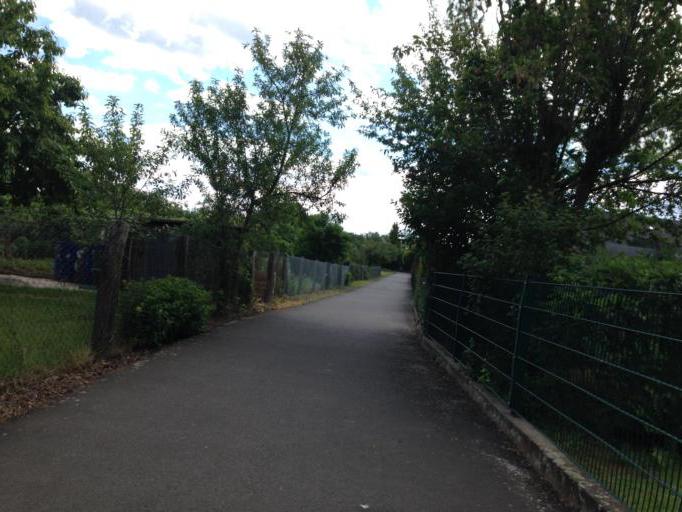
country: DE
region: Hesse
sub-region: Regierungsbezirk Giessen
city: Heuchelheim
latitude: 50.5862
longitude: 8.6298
